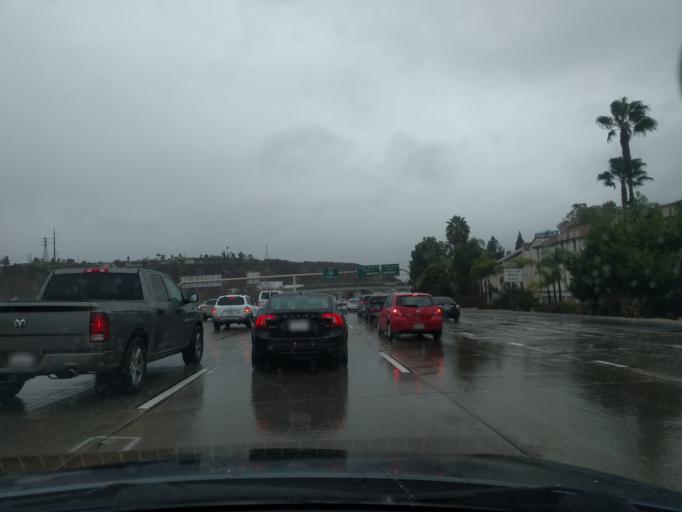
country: US
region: California
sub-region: San Diego County
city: San Diego
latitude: 32.7836
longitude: -117.1139
